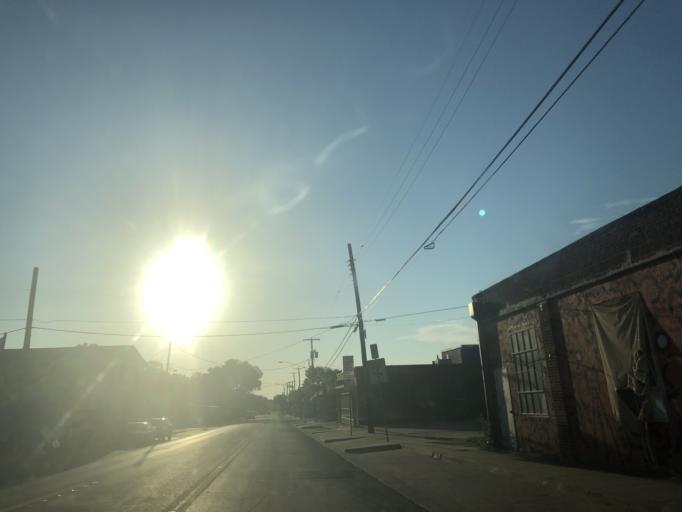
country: US
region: Texas
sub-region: Dallas County
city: Dallas
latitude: 32.7494
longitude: -96.8315
